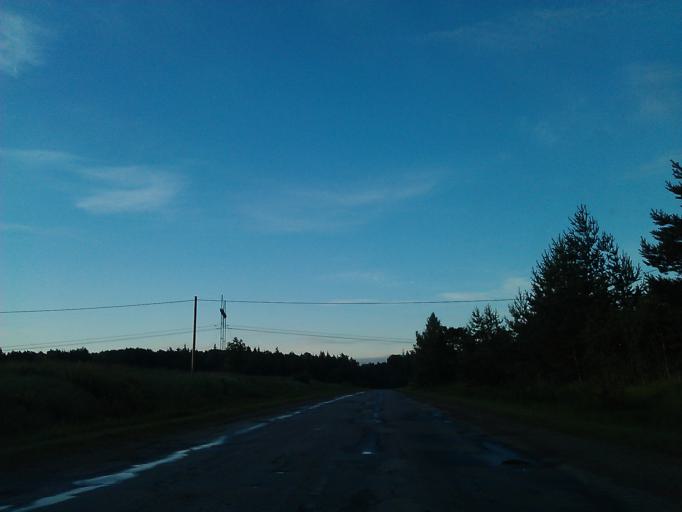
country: LV
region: Pargaujas
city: Stalbe
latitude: 57.3630
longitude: 25.0612
